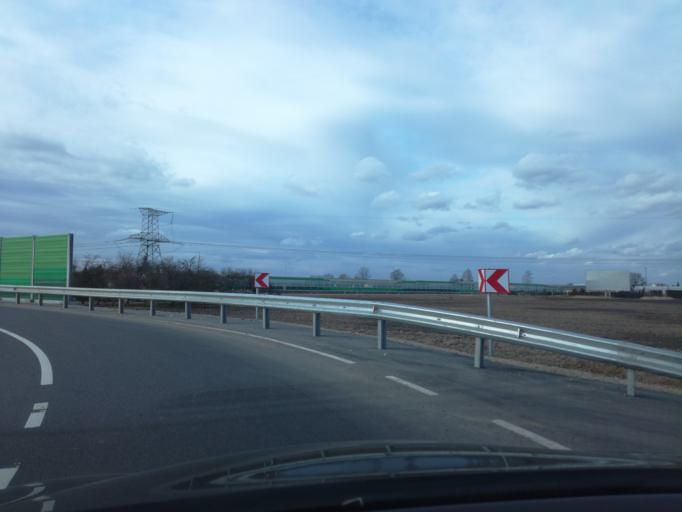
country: LT
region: Marijampoles apskritis
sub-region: Marijampole Municipality
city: Marijampole
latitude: 54.5945
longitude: 23.3971
